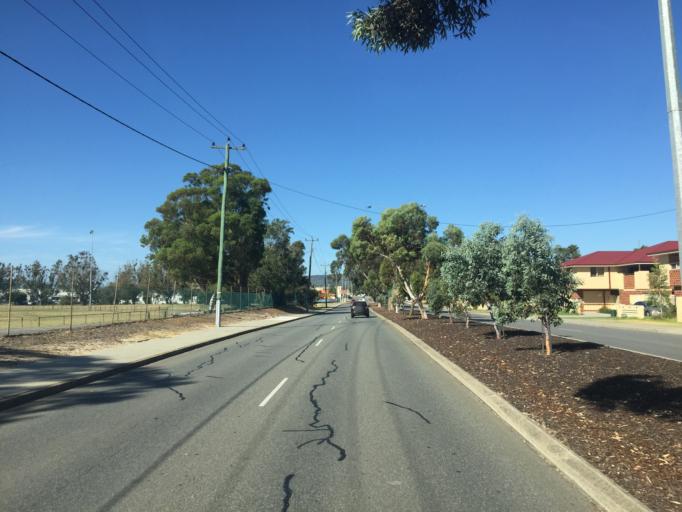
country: AU
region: Western Australia
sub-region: Gosnells
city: Maddington
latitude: -32.0477
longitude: 115.9866
